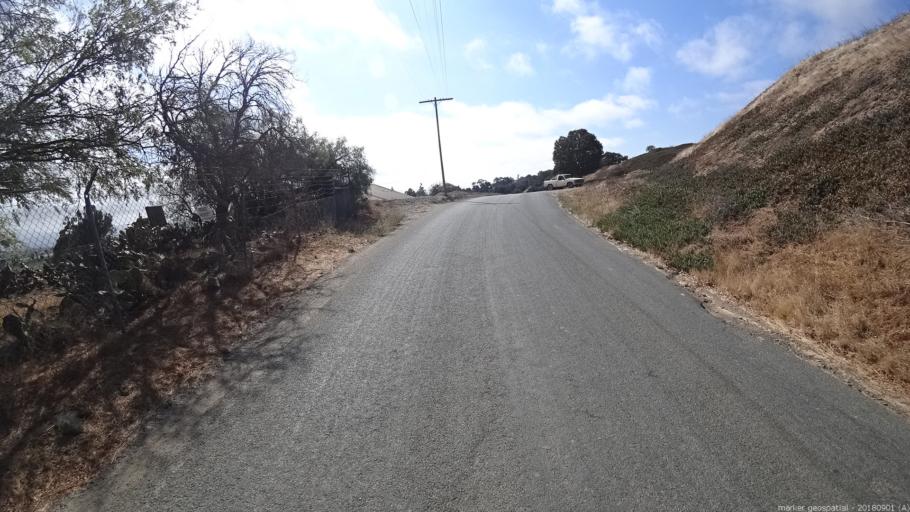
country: US
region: California
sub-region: Monterey County
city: Soledad
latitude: 36.3939
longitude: -121.3687
